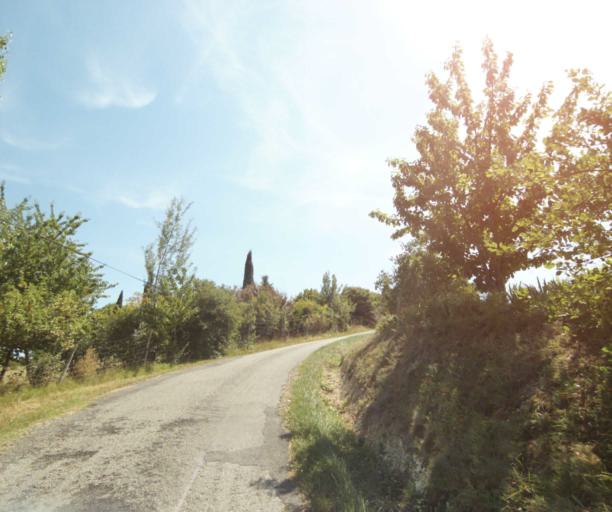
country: FR
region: Midi-Pyrenees
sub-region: Departement de l'Ariege
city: Lezat-sur-Leze
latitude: 43.2487
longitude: 1.3814
